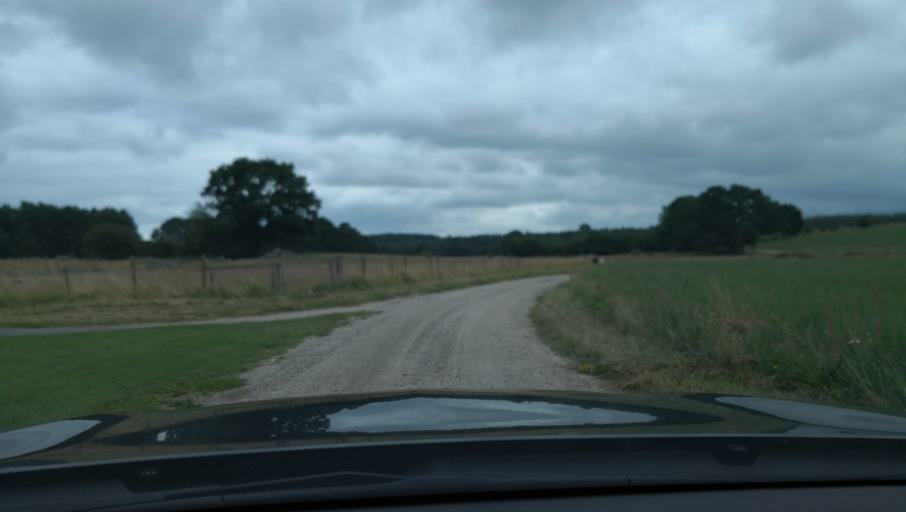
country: SE
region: Skane
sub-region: Simrishamns Kommun
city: Kivik
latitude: 55.7251
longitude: 14.1678
